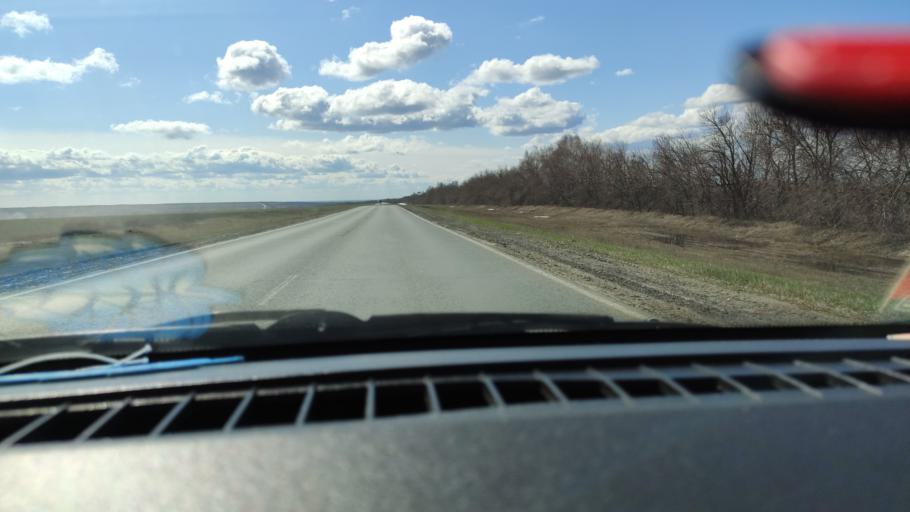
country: RU
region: Saratov
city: Dukhovnitskoye
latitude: 52.7709
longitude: 48.2364
